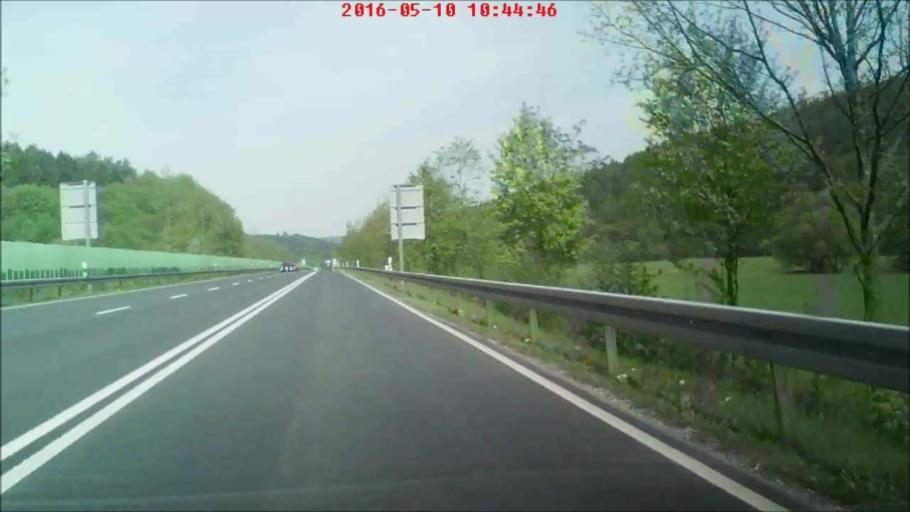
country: DE
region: Hesse
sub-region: Regierungsbezirk Kassel
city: Burghaun
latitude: 50.7234
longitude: 9.7075
